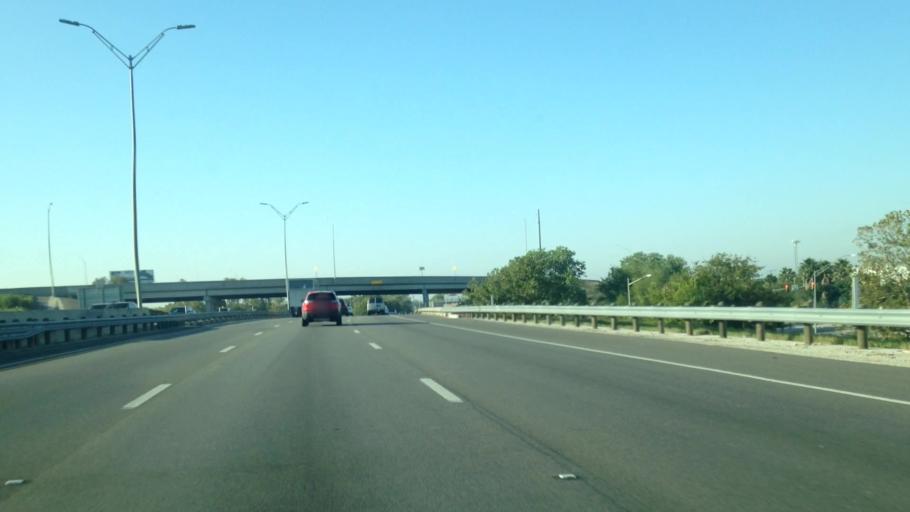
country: US
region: Texas
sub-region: Bexar County
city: Kirby
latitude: 29.4571
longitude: -98.4128
